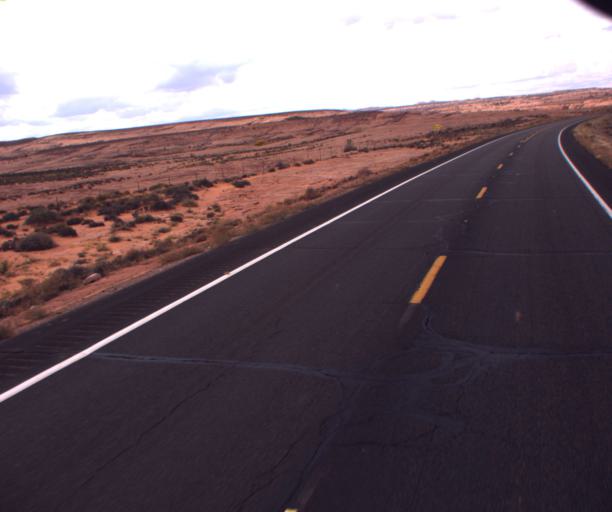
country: US
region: Arizona
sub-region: Apache County
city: Many Farms
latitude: 36.9390
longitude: -109.6986
